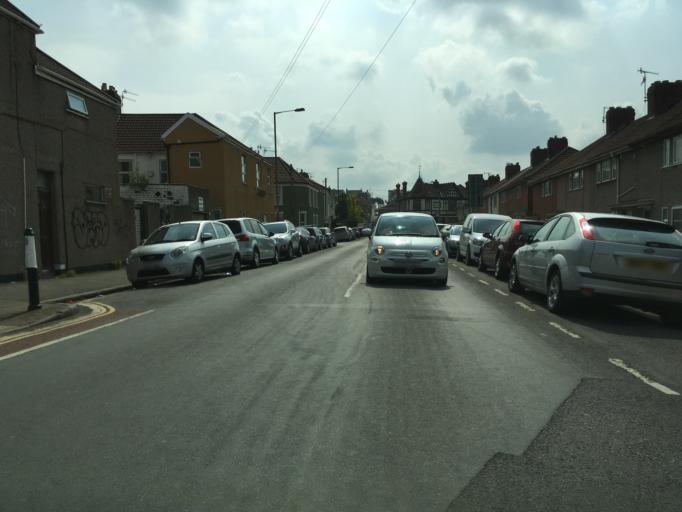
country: GB
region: England
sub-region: Bristol
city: Bristol
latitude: 51.4367
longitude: -2.6128
